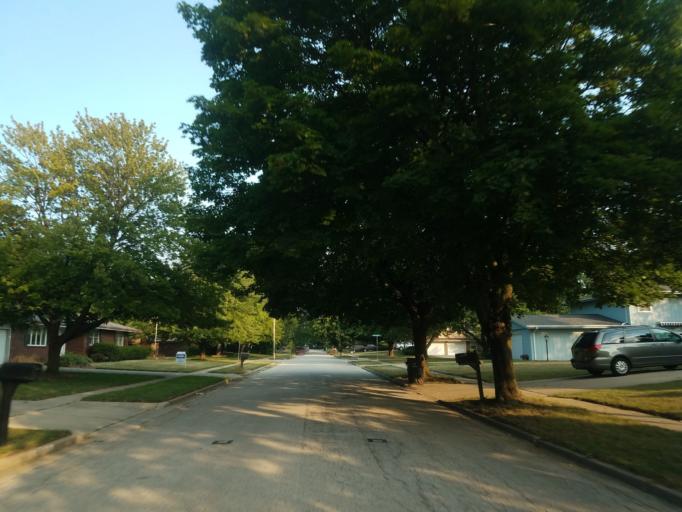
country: US
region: Illinois
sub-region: McLean County
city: Bloomington
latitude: 40.4704
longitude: -88.9461
